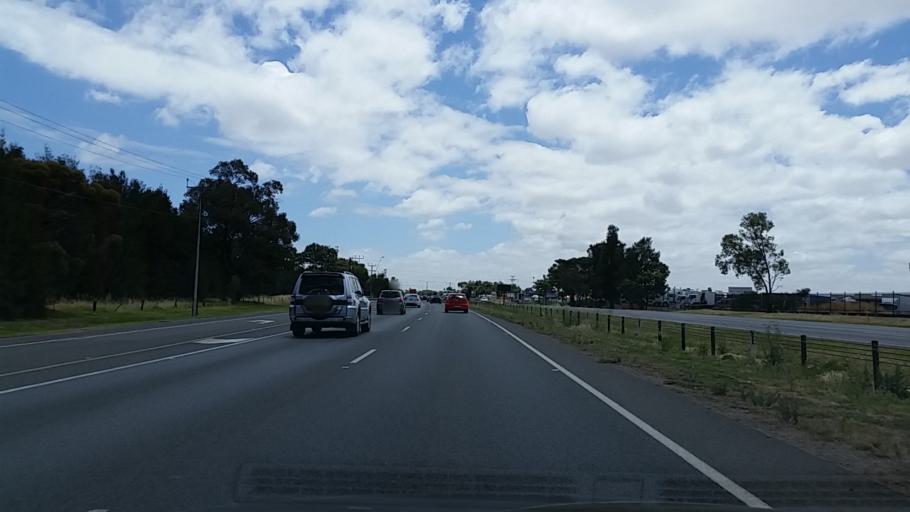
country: AU
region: South Australia
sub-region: Salisbury
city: Salisbury
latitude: -34.7930
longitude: 138.5966
